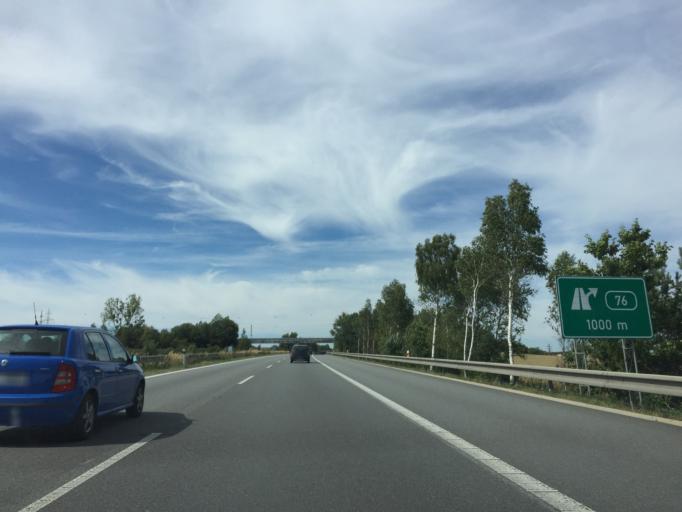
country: CZ
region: Jihocesky
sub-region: Okres Tabor
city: Sezimovo Usti
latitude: 49.4159
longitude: 14.7084
